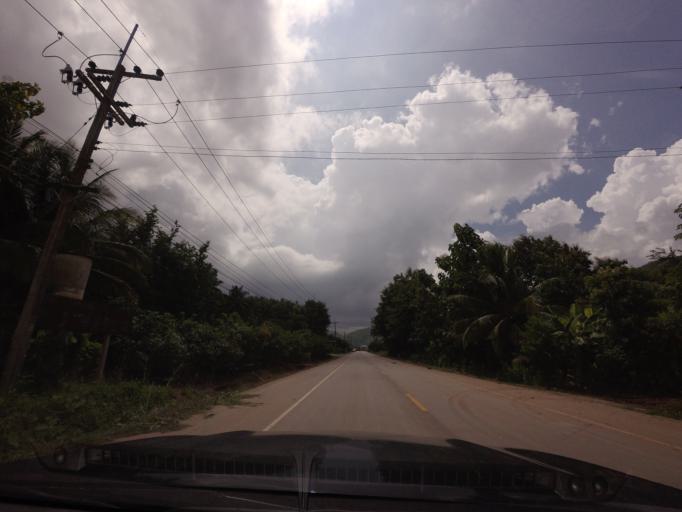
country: LA
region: Vientiane
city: Muang Sanakham
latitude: 17.9936
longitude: 101.7498
